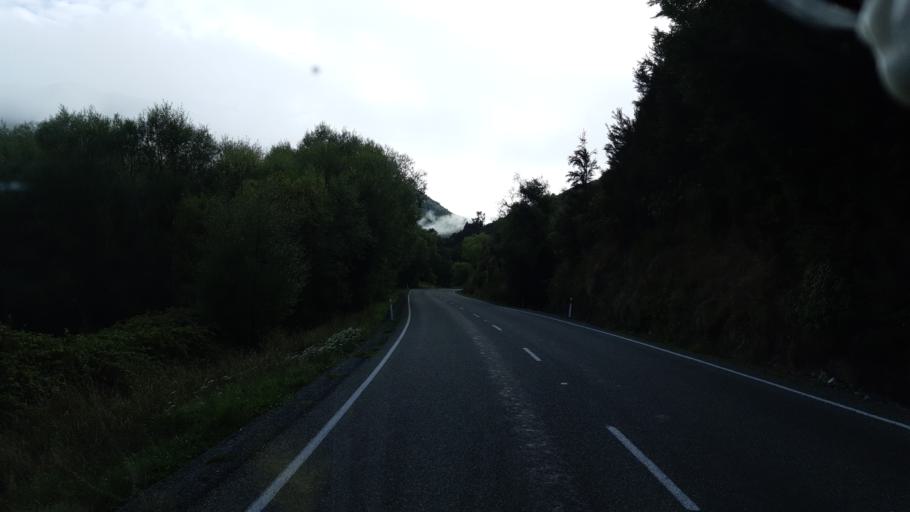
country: NZ
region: West Coast
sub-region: Buller District
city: Westport
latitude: -42.0565
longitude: 172.2561
